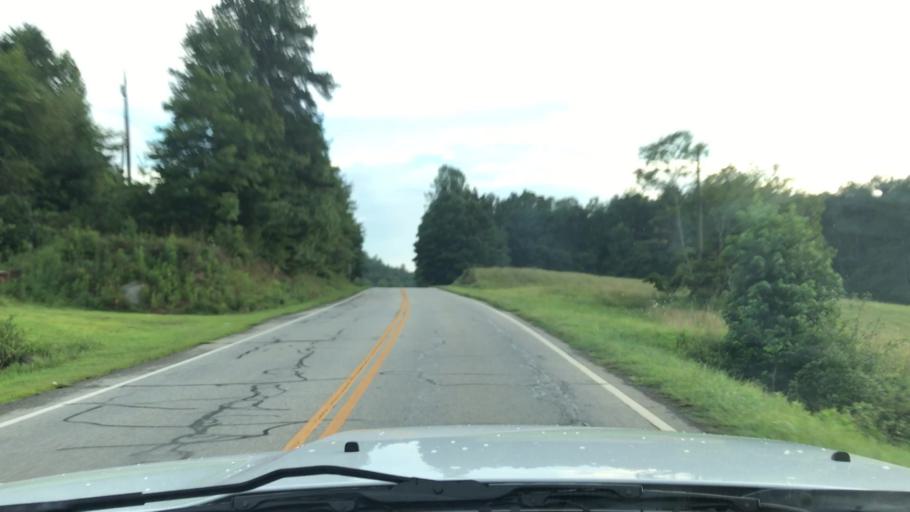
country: US
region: Georgia
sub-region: Fannin County
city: Blue Ridge
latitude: 34.9500
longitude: -84.2368
